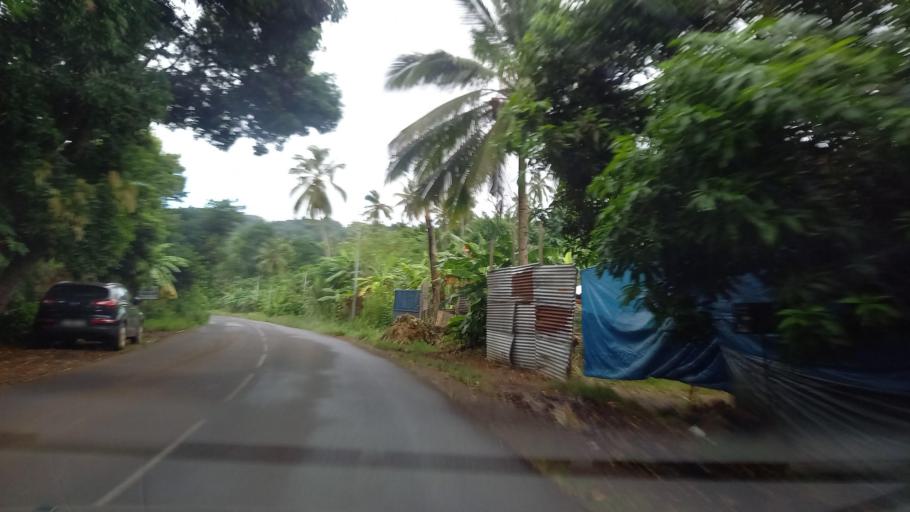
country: YT
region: Sada
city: Sada
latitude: -12.8712
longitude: 45.1179
